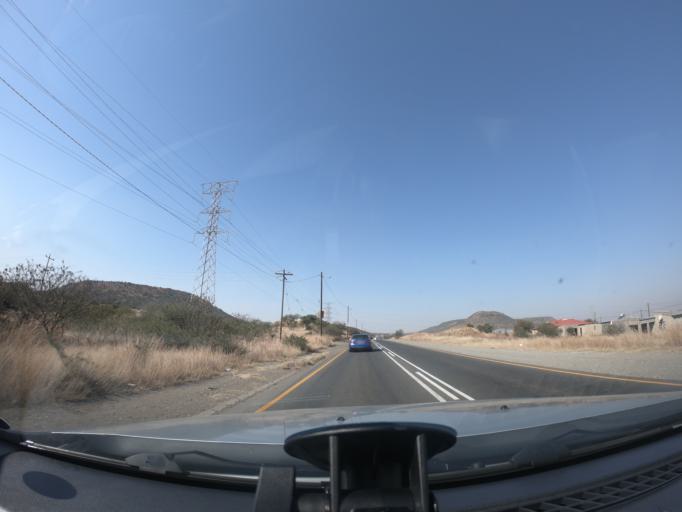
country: ZA
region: KwaZulu-Natal
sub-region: uThukela District Municipality
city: Ladysmith
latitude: -28.5528
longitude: 29.8339
